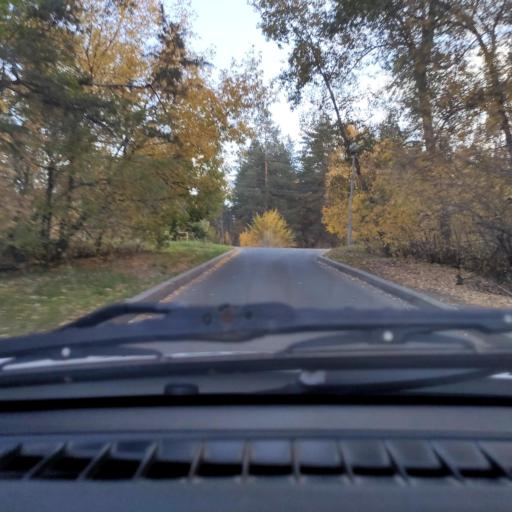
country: RU
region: Samara
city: Zhigulevsk
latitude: 53.4870
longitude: 49.4660
